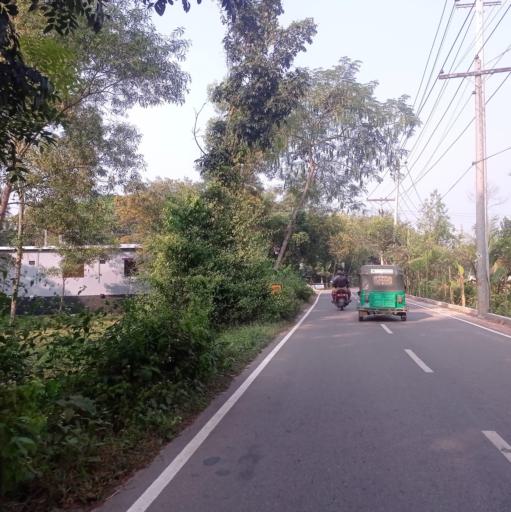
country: BD
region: Dhaka
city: Bhairab Bazar
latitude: 24.0749
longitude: 90.8463
